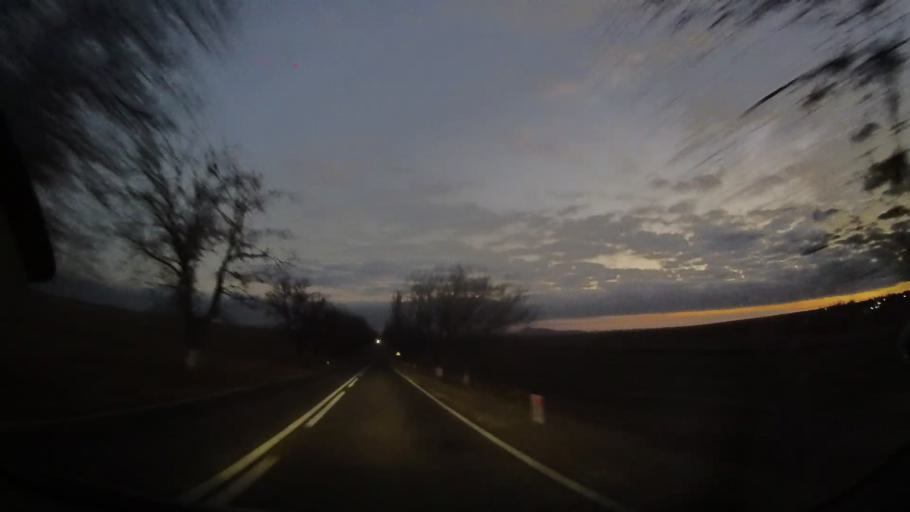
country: RO
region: Tulcea
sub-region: Comuna Frecatei
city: Cataloi
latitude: 45.0913
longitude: 28.7412
